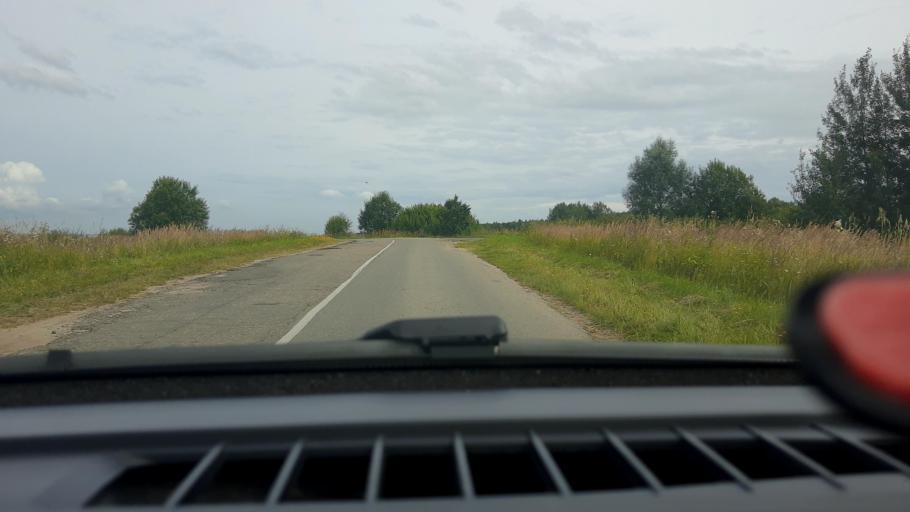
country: RU
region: Nizjnij Novgorod
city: Burevestnik
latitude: 56.0436
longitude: 43.7144
